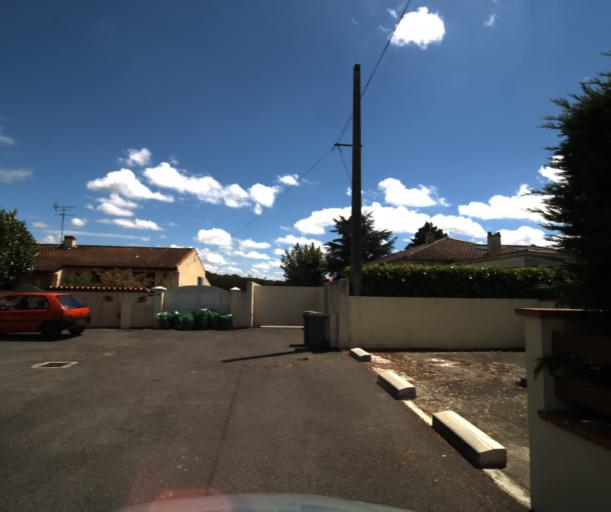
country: FR
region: Midi-Pyrenees
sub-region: Departement de la Haute-Garonne
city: Lacroix-Falgarde
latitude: 43.4948
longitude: 1.4041
